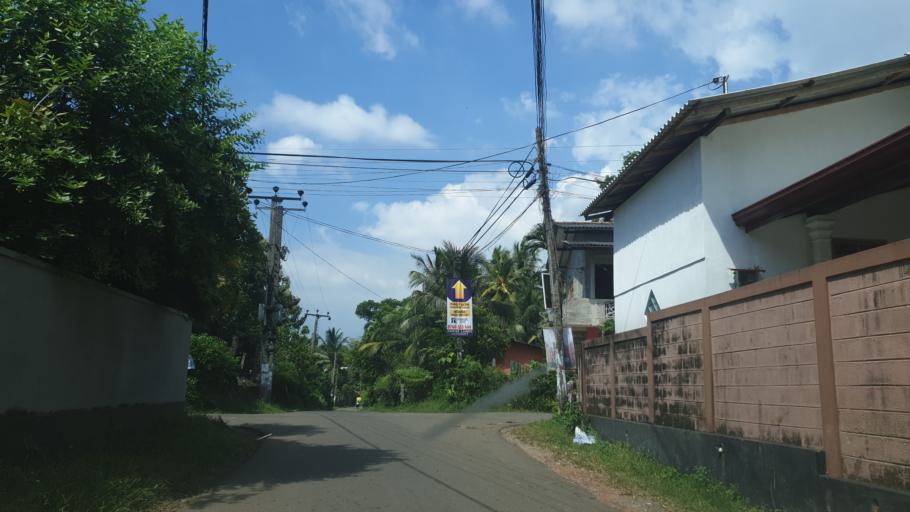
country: LK
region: Western
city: Horana South
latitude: 6.7054
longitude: 79.9846
